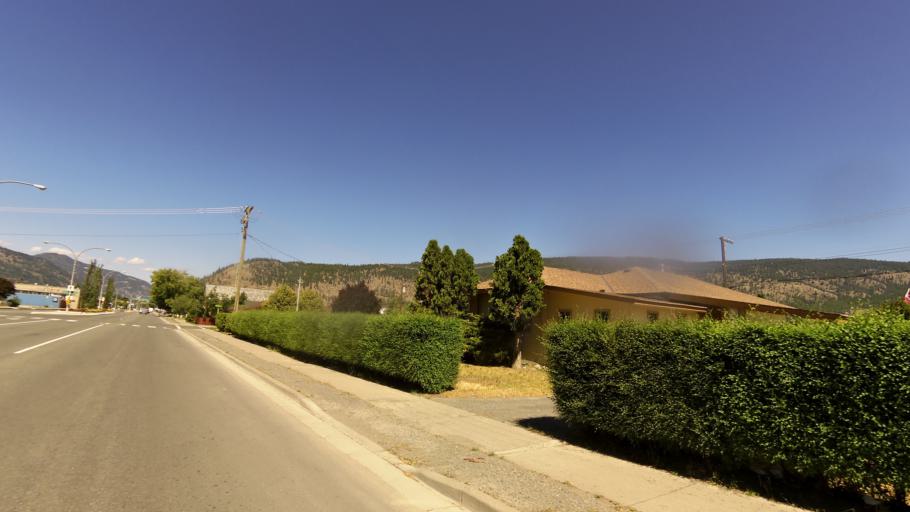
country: CA
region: British Columbia
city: Merritt
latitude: 50.1105
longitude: -120.7831
